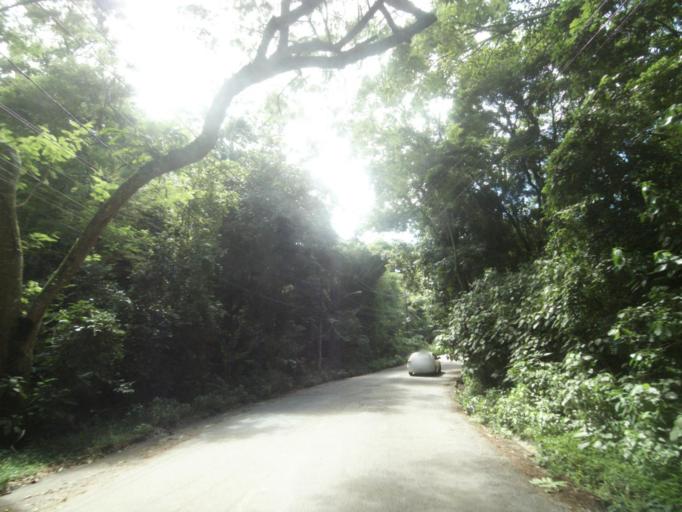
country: BR
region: Rio de Janeiro
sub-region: Niteroi
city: Niteroi
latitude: -22.9631
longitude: -43.0239
